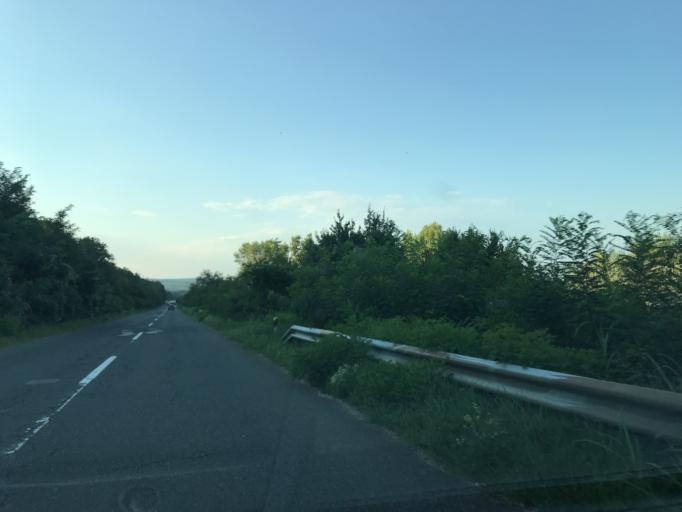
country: RO
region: Mehedinti
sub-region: Comuna Gogosu
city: Ostrovu Mare
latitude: 44.4552
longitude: 22.4524
